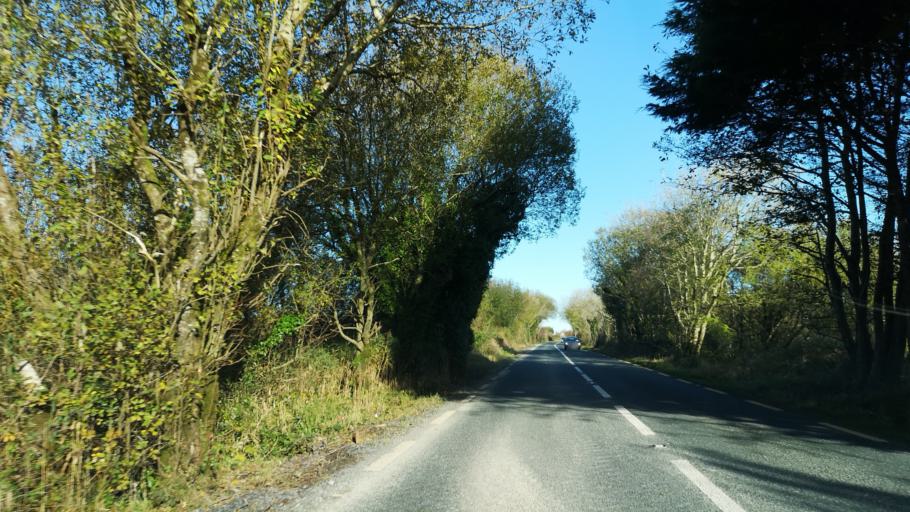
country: IE
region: Connaught
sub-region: County Galway
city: Claregalway
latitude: 53.3975
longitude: -9.0175
